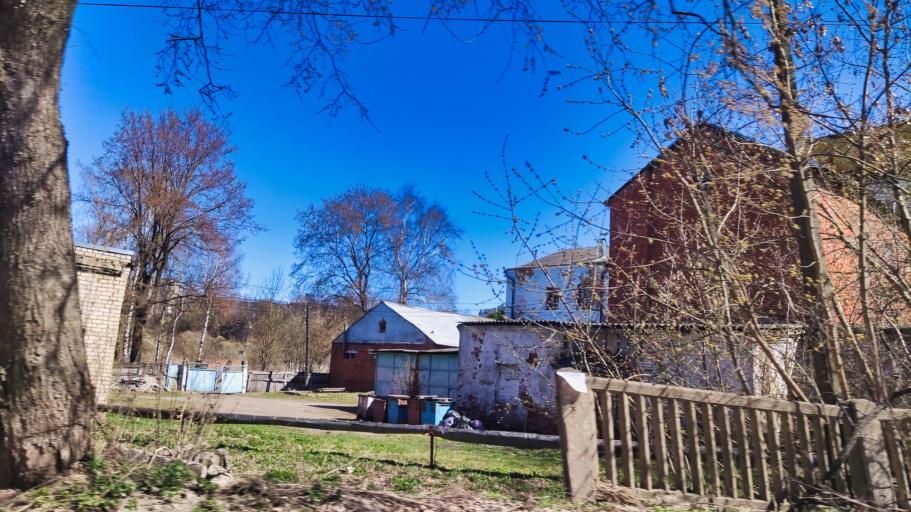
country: RU
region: Tverskaya
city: Rzhev
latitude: 56.2573
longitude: 34.3361
